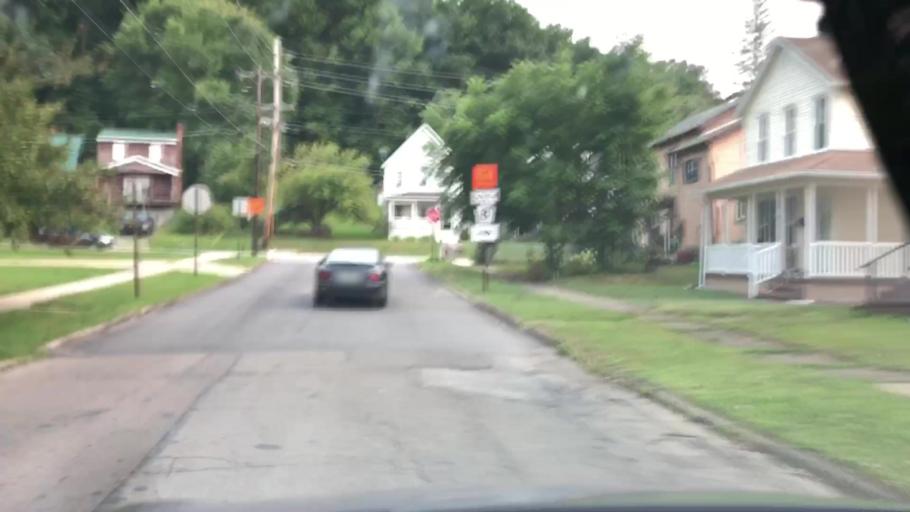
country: US
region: Pennsylvania
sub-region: Crawford County
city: Titusville
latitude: 41.6226
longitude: -79.6696
